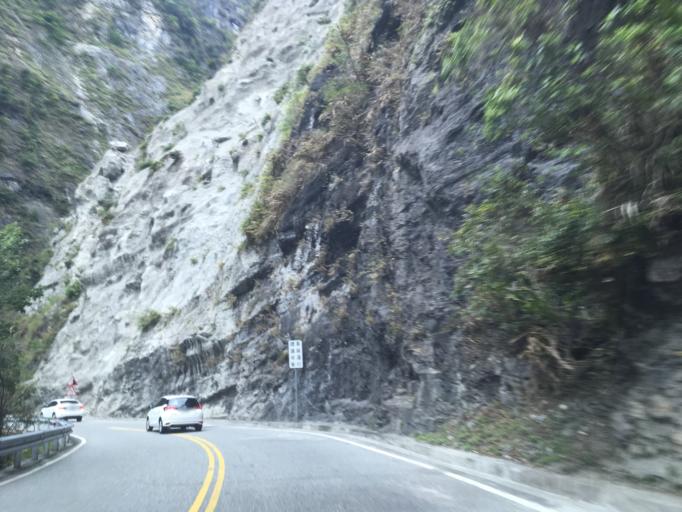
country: TW
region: Taiwan
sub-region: Hualien
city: Hualian
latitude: 24.1742
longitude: 121.5238
